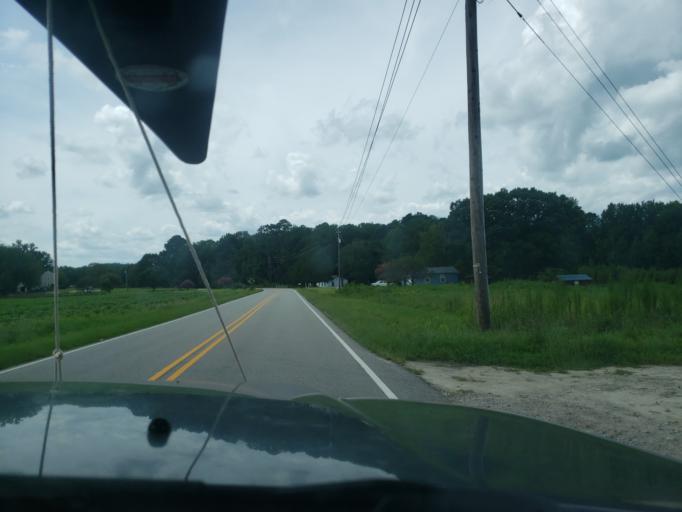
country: US
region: North Carolina
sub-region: Wake County
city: Zebulon
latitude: 35.8819
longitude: -78.3683
